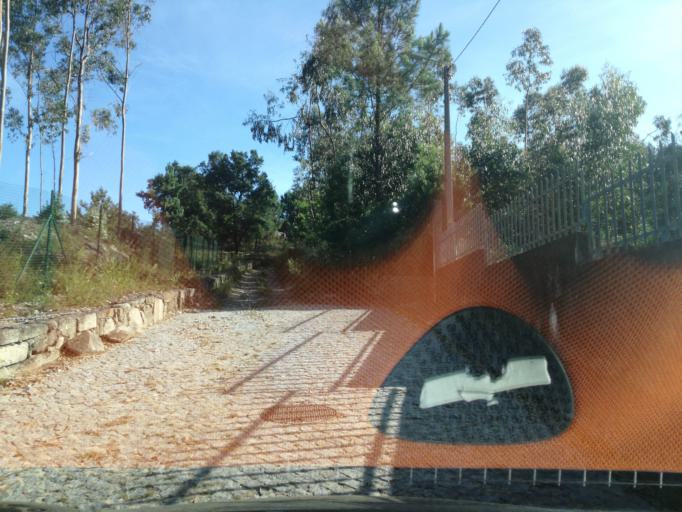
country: PT
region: Porto
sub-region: Maia
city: Anta
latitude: 41.2865
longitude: -8.6098
